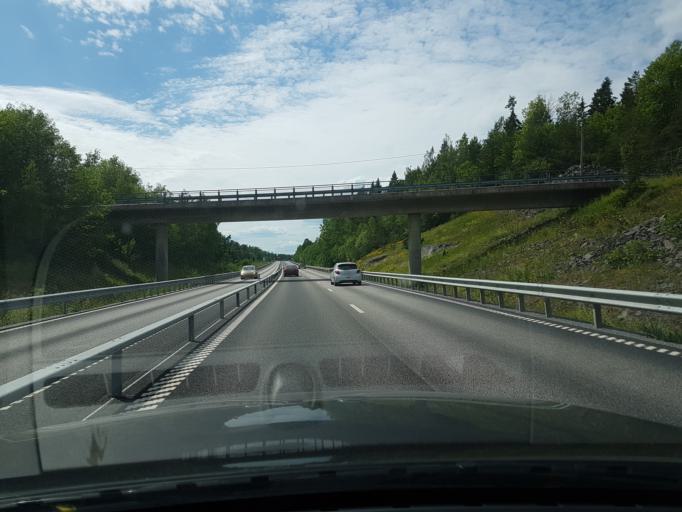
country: SE
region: Stockholm
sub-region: Norrtalje Kommun
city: Bjorko
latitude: 59.7205
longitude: 18.9452
